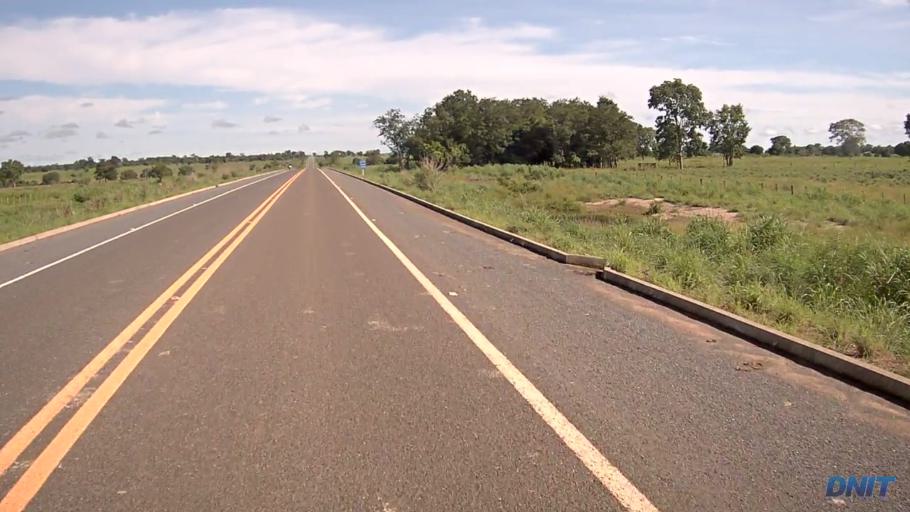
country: BR
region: Goias
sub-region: Sao Miguel Do Araguaia
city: Sao Miguel do Araguaia
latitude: -13.4604
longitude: -50.1178
